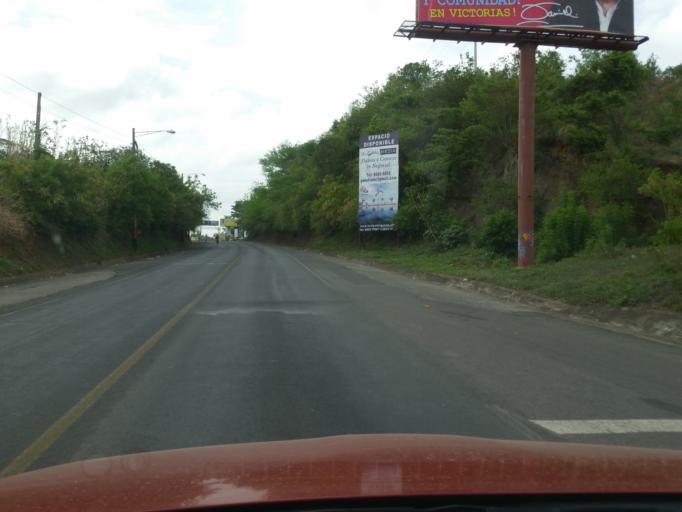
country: NI
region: Masaya
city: Nindiri
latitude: 11.9945
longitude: -86.1060
